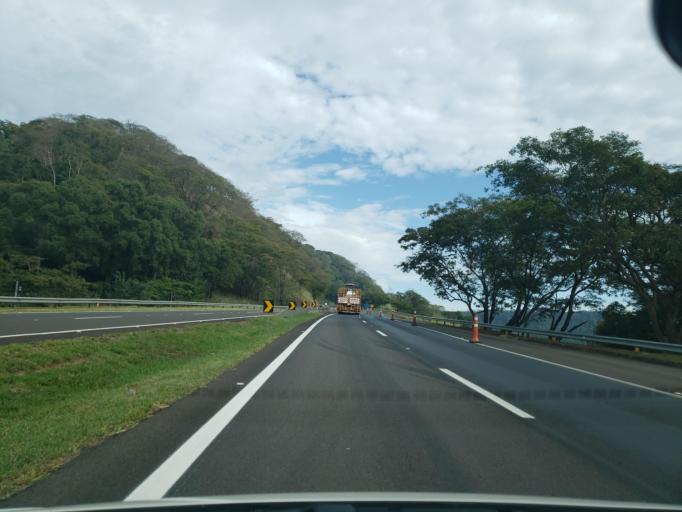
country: BR
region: Sao Paulo
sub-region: Dois Corregos
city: Dois Corregos
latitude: -22.2492
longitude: -48.3424
